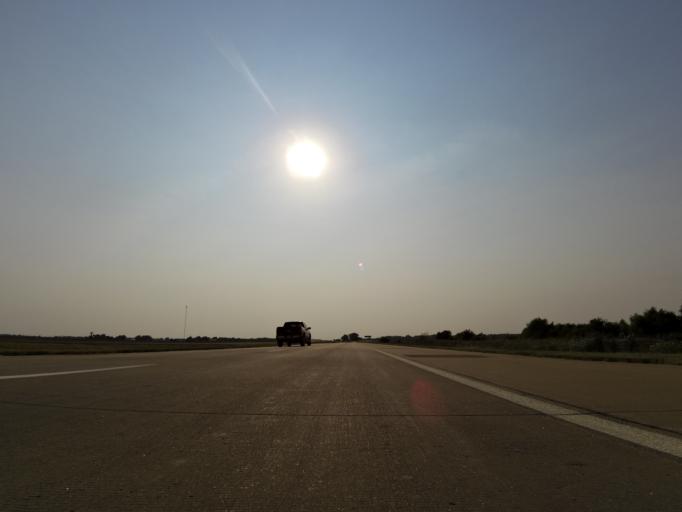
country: US
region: Kansas
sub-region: Reno County
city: Haven
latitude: 37.8764
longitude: -97.6748
